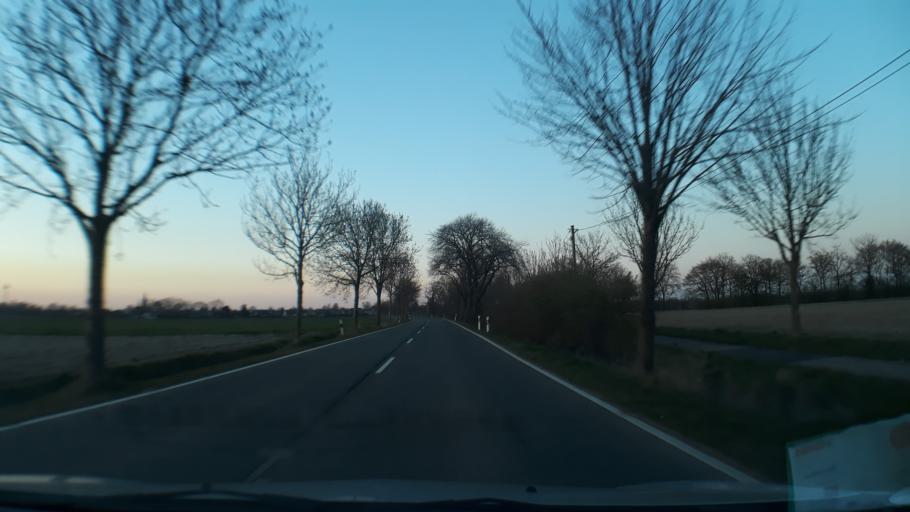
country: DE
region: North Rhine-Westphalia
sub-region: Regierungsbezirk Koln
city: Norvenich
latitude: 50.8033
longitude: 6.5867
